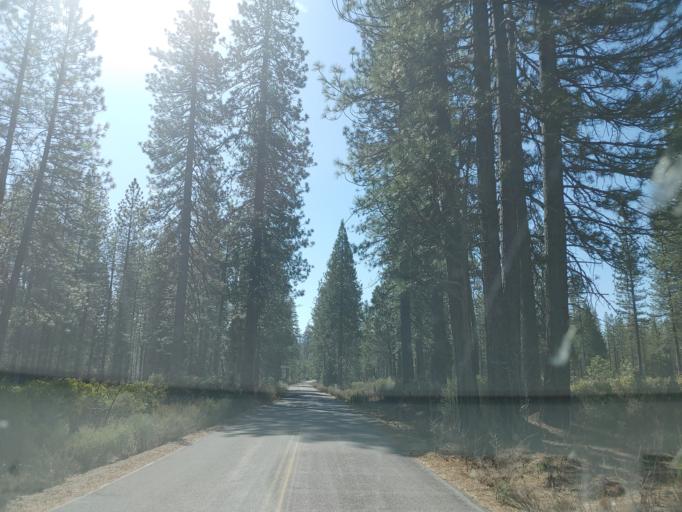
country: US
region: California
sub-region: Siskiyou County
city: McCloud
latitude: 41.2535
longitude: -122.0297
